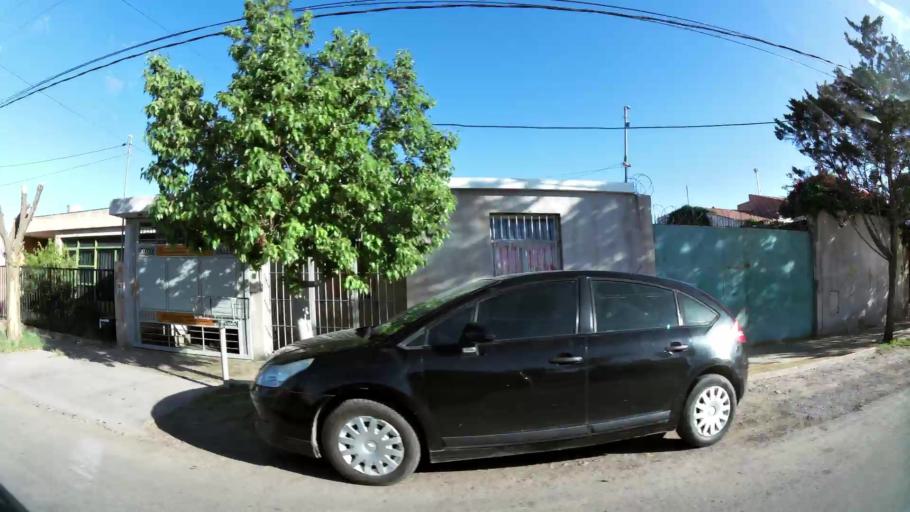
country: AR
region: San Juan
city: Villa Krause
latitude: -31.5590
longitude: -68.5172
